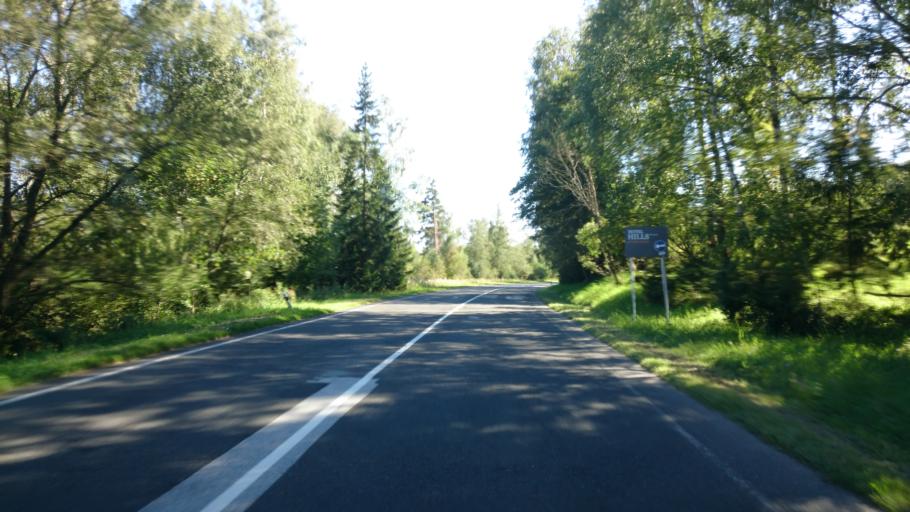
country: SK
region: Presovsky
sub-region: Okres Poprad
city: Vysoke Tatry
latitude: 49.1590
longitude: 20.2727
